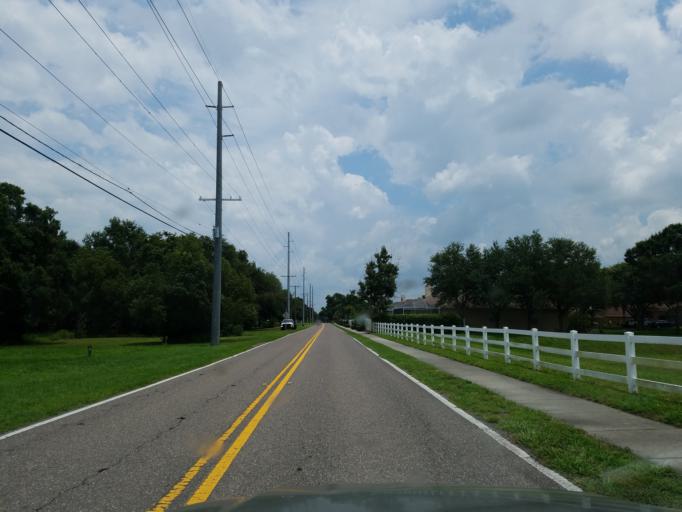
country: US
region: Florida
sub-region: Hillsborough County
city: Valrico
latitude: 27.9231
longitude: -82.2353
